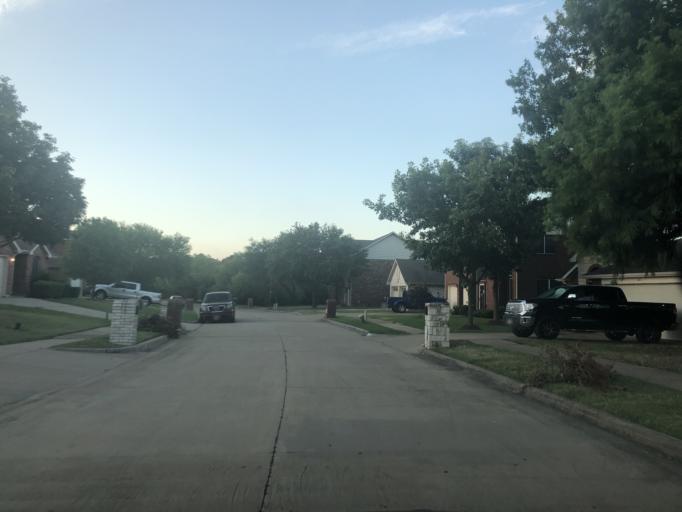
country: US
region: Texas
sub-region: Dallas County
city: Cedar Hill
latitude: 32.6489
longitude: -96.9737
